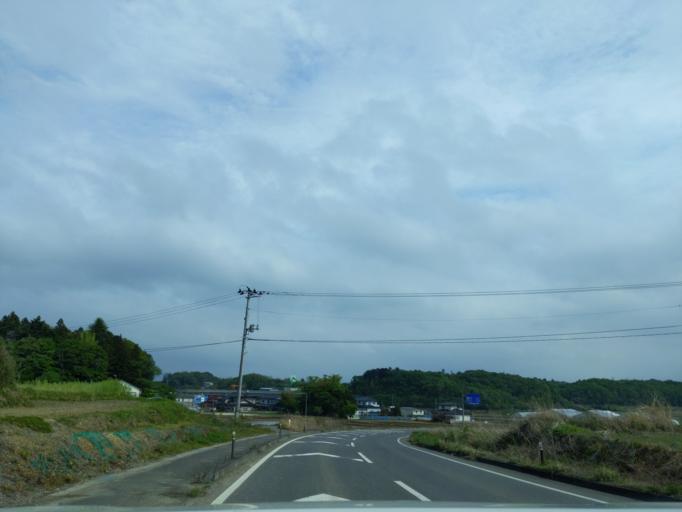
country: JP
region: Fukushima
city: Sukagawa
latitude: 37.3260
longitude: 140.3518
